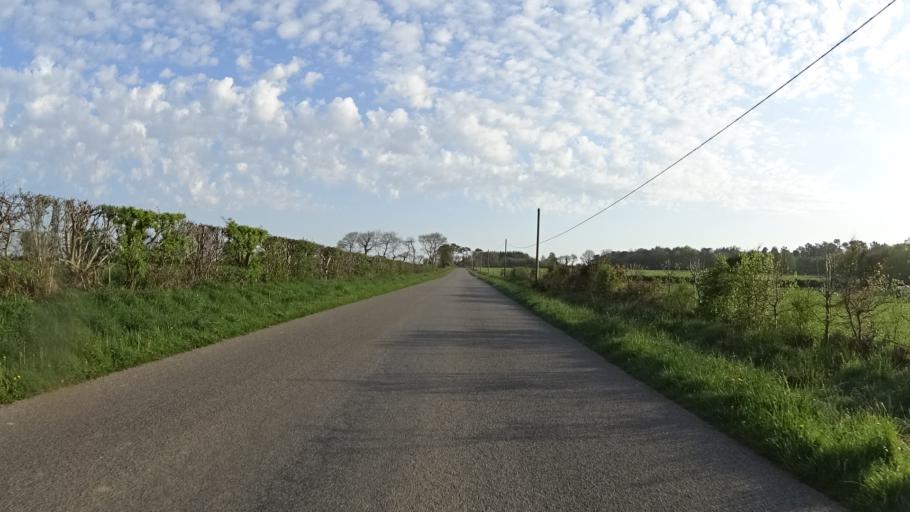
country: FR
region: Brittany
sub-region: Departement du Finistere
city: Sizun
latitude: 48.4230
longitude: -4.0747
